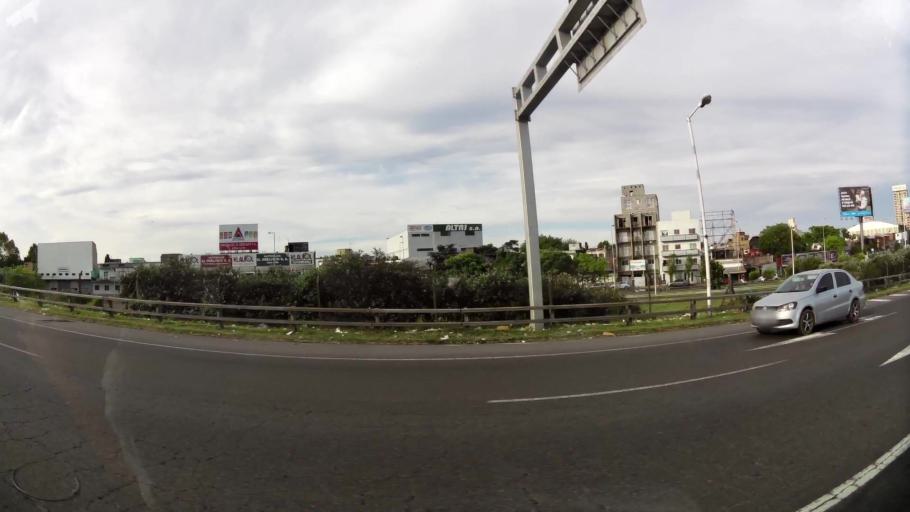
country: AR
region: Buenos Aires
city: Caseros
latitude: -34.6349
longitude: -58.5370
